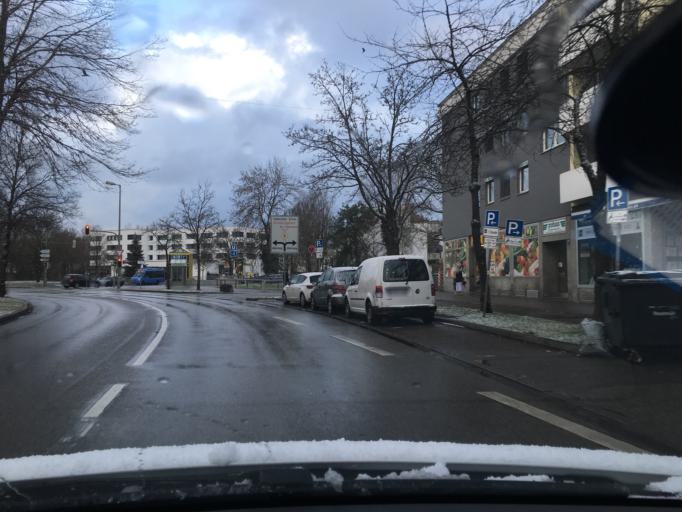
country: DE
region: Bavaria
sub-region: Upper Bavaria
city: Munich
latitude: 48.1020
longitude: 11.5460
